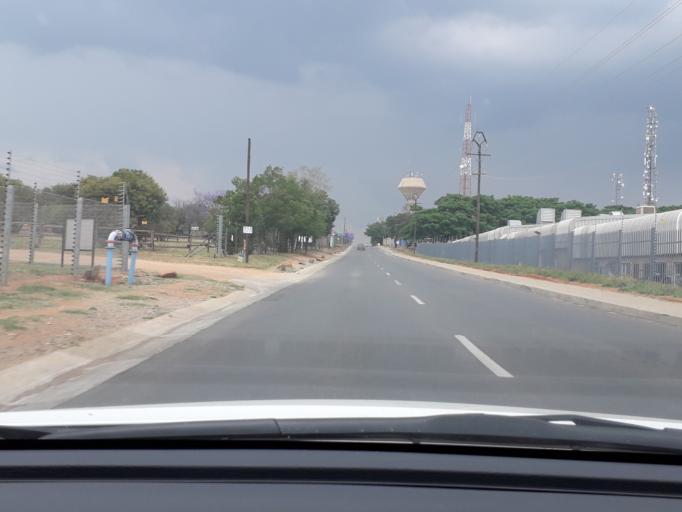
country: ZA
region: Gauteng
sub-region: West Rand District Municipality
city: Muldersdriseloop
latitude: -26.0747
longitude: 27.9250
